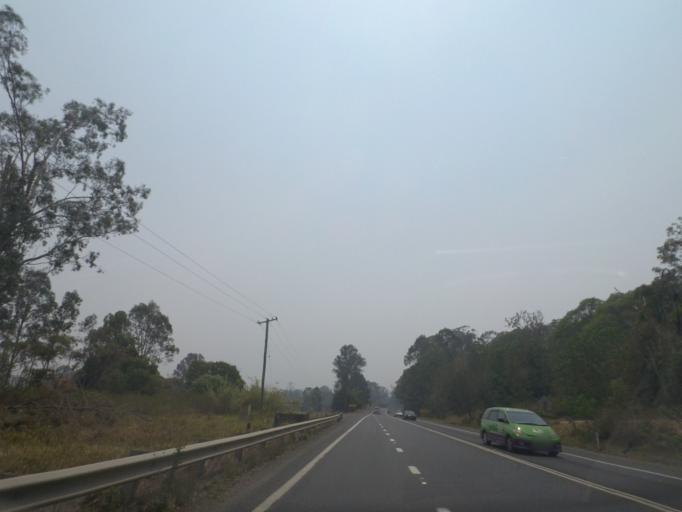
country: AU
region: New South Wales
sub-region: Clarence Valley
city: Maclean
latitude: -29.5554
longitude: 153.1519
